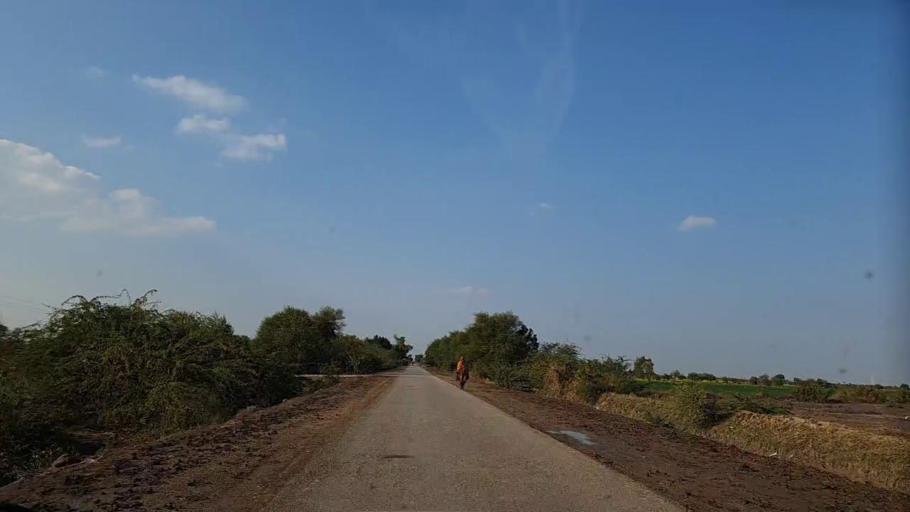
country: PK
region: Sindh
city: Pithoro
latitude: 25.7255
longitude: 69.2147
